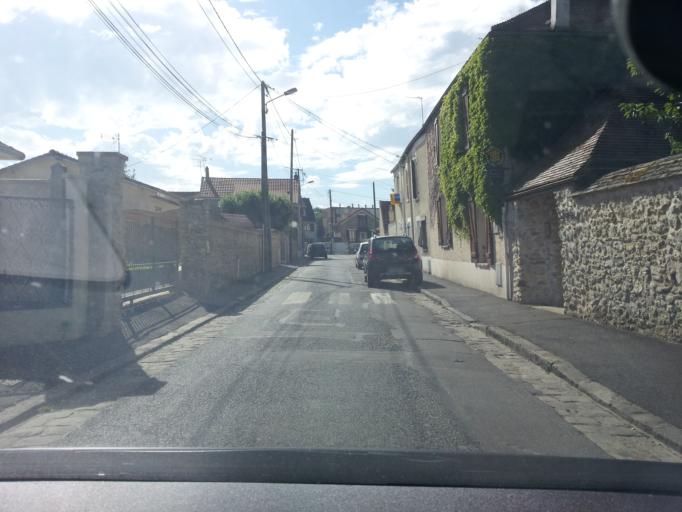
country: FR
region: Ile-de-France
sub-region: Departement de l'Essonne
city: Ballancourt-sur-Essonne
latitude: 48.5277
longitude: 2.3779
